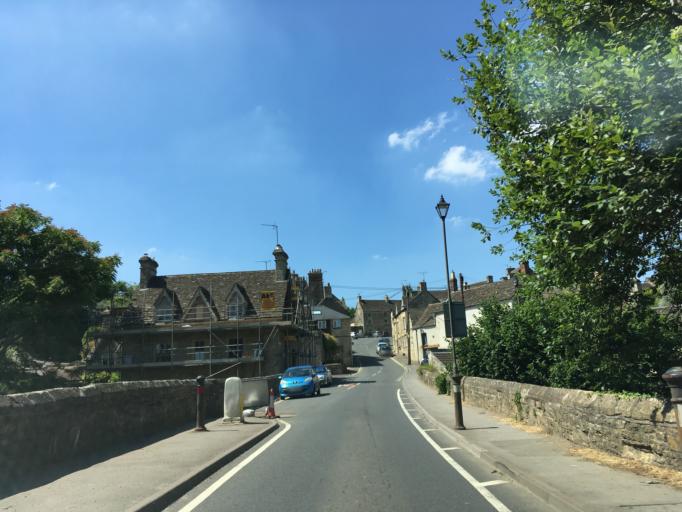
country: GB
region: England
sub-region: Gloucestershire
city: Tetbury
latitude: 51.6354
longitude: -2.1564
